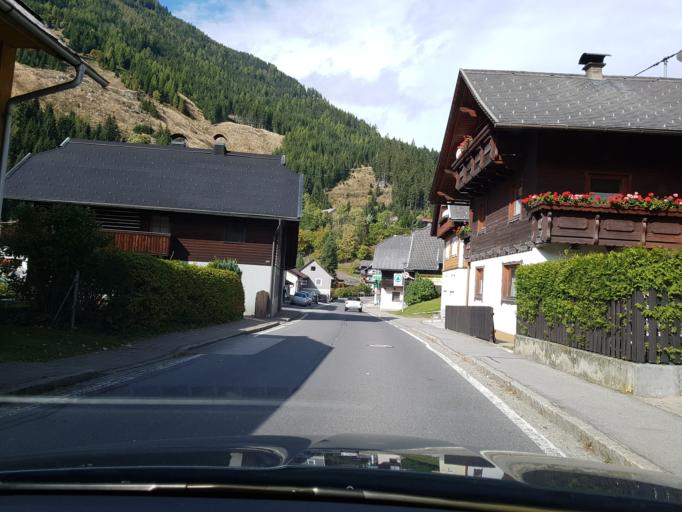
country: AT
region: Carinthia
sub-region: Politischer Bezirk Feldkirchen
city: Gnesau
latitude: 46.8551
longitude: 13.8931
